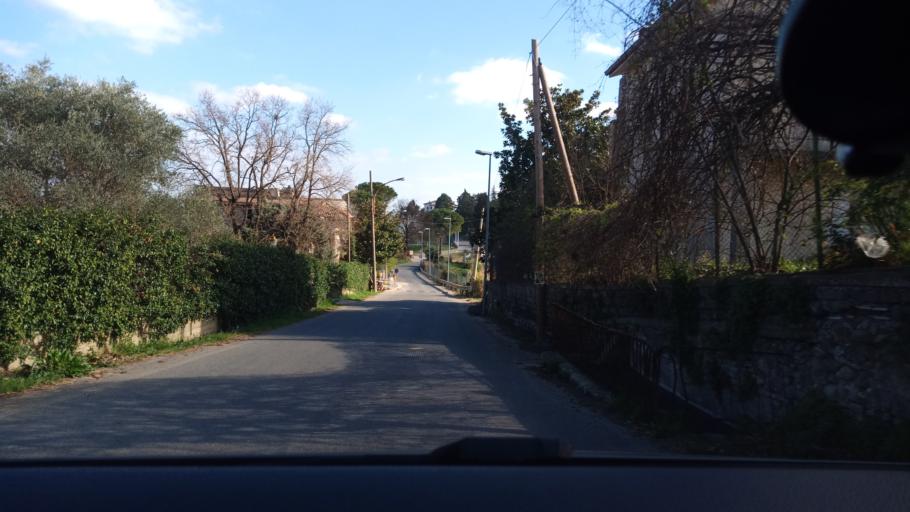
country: IT
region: Latium
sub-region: Citta metropolitana di Roma Capitale
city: Torrita Tiberina
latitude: 42.2412
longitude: 12.6144
